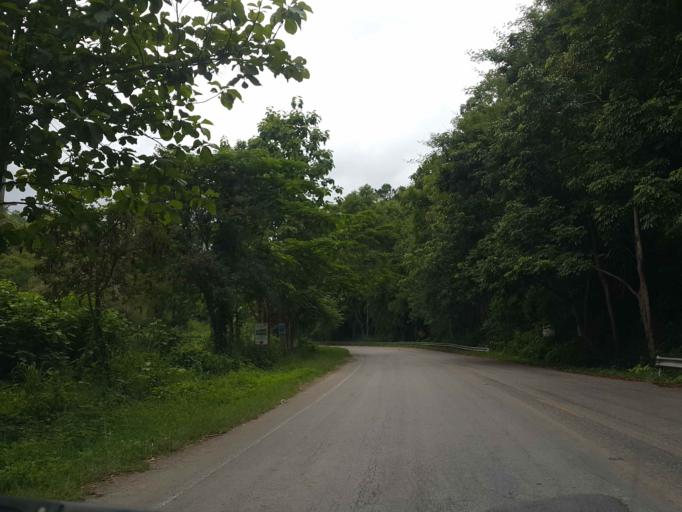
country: TH
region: Chiang Mai
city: Samoeng
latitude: 18.8046
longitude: 98.8296
